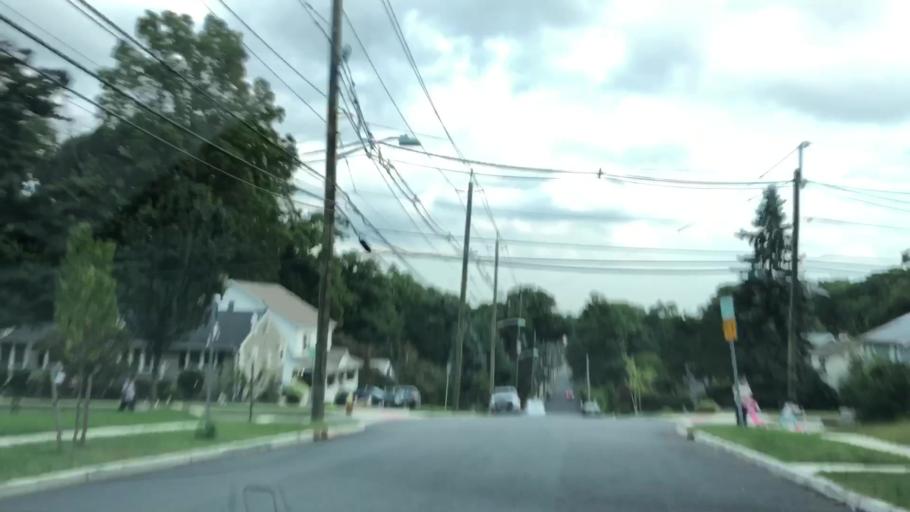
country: US
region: New Jersey
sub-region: Essex County
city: Upper Montclair
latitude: 40.8583
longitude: -74.1955
